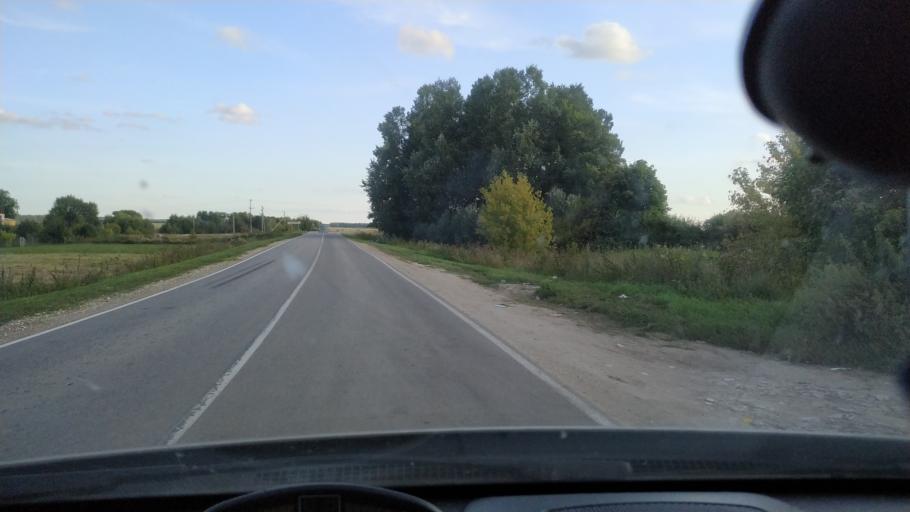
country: RU
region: Rjazan
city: Rybnoye
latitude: 54.8643
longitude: 39.6484
